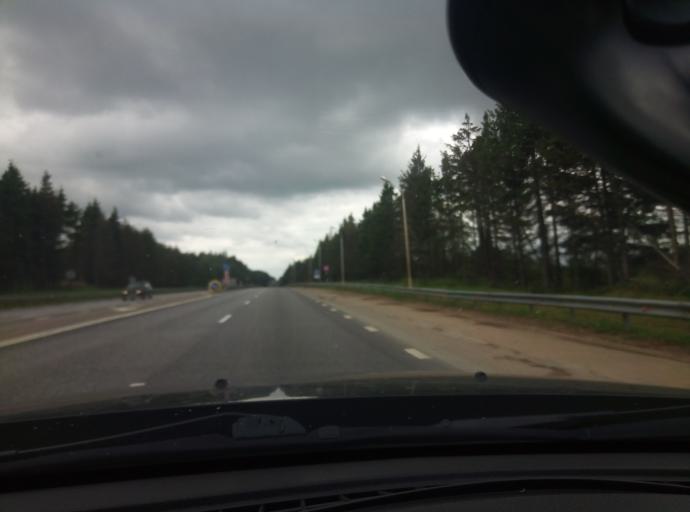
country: RU
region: Kaluga
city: Maloyaroslavets
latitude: 55.0071
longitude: 36.5389
